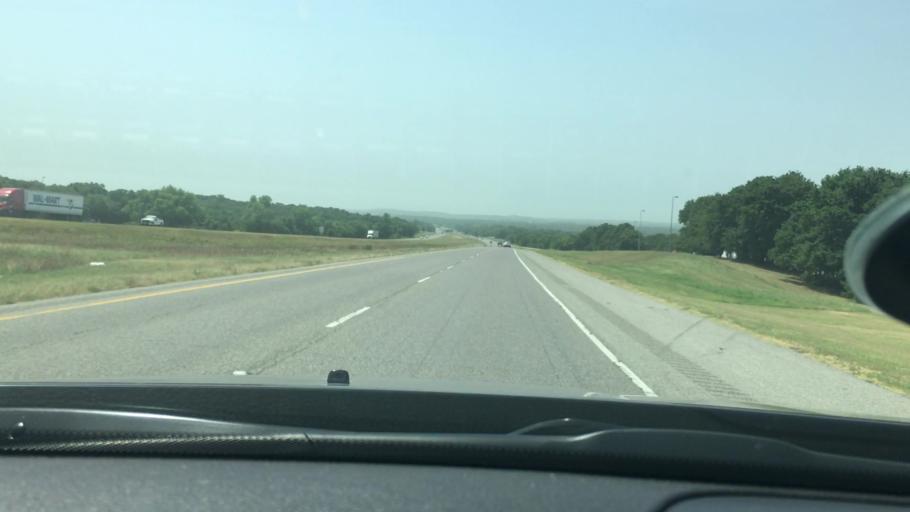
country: US
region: Oklahoma
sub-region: Murray County
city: Davis
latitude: 34.5507
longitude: -97.1913
